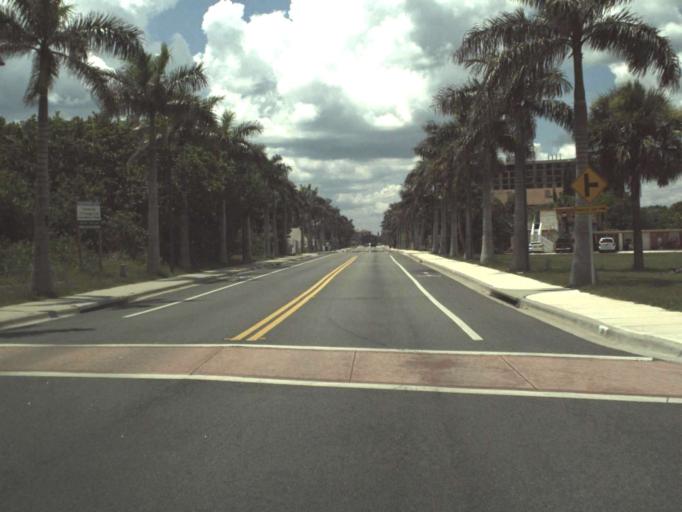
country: US
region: Florida
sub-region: Saint Lucie County
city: Fort Pierce
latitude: 27.4641
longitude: -80.2901
